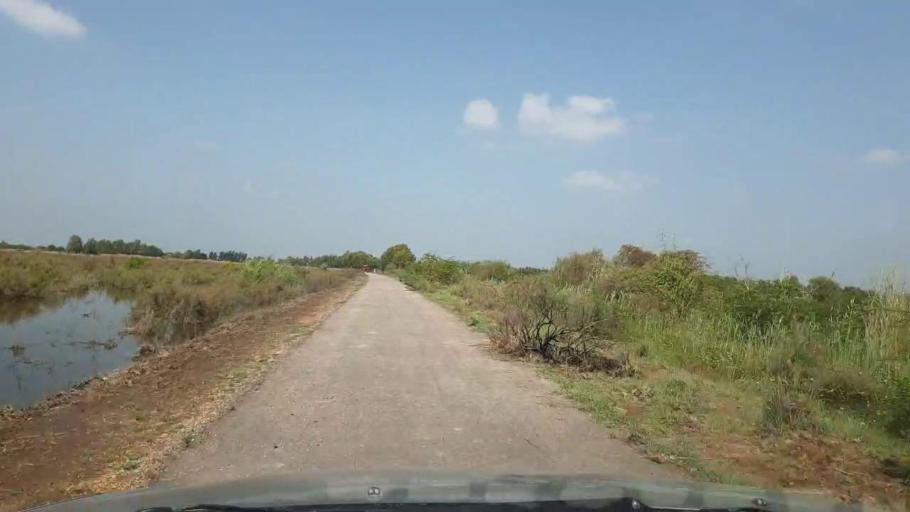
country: PK
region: Sindh
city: Rajo Khanani
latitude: 25.0328
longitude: 68.9364
